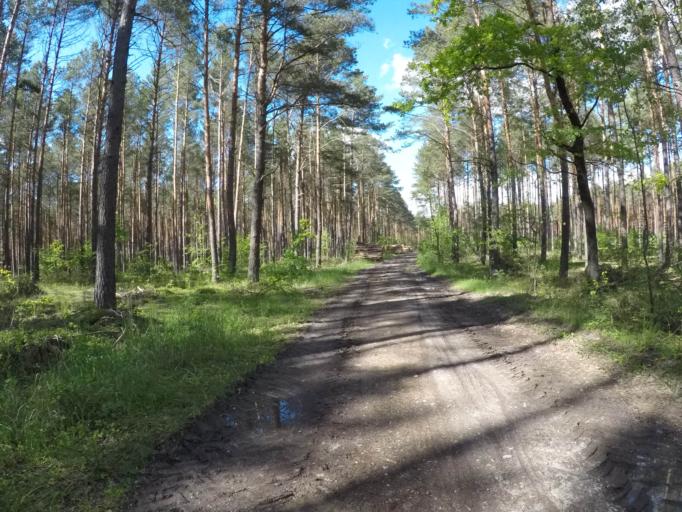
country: PL
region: Swietokrzyskie
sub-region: Powiat kielecki
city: Kostomloty Drugie
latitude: 50.8884
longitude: 20.5377
